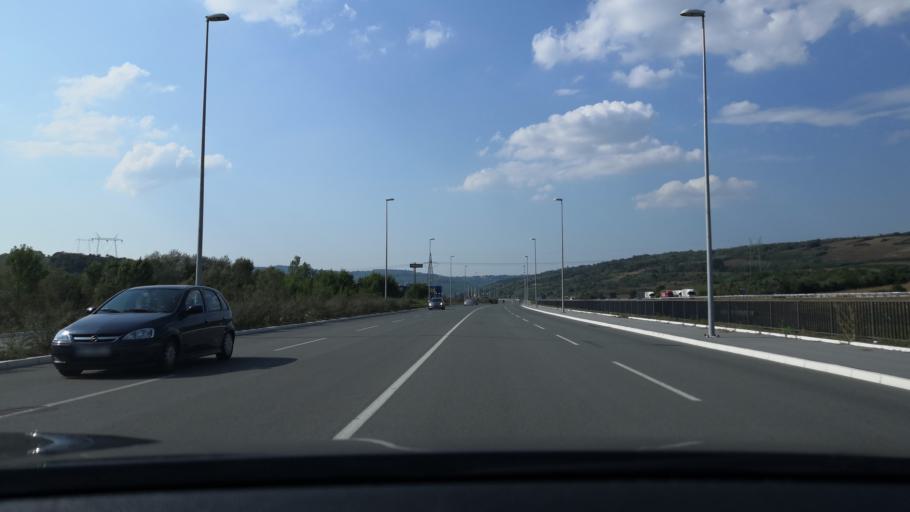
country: RS
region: Central Serbia
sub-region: Belgrade
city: Zvezdara
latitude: 44.7064
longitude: 20.5697
